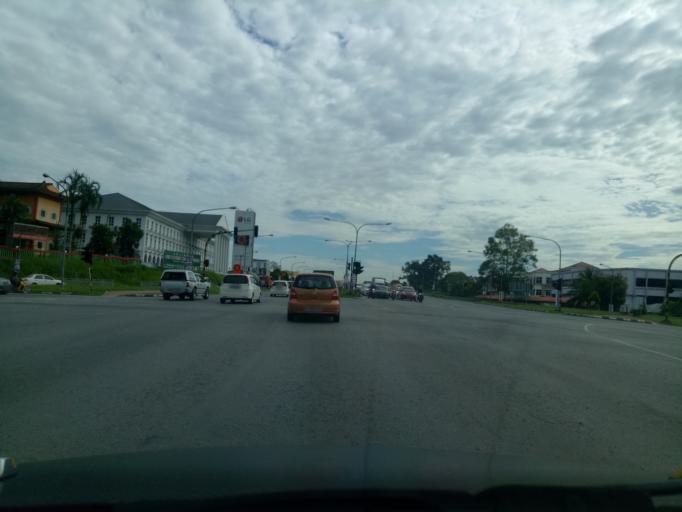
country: MY
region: Sarawak
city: Kuching
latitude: 1.4687
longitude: 110.3284
